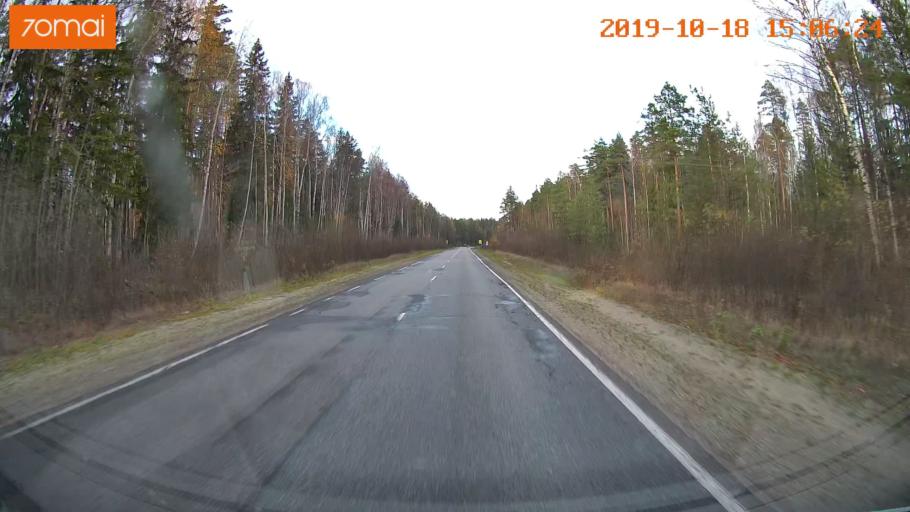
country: RU
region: Vladimir
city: Gus'-Khrustal'nyy
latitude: 55.5295
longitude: 40.5783
